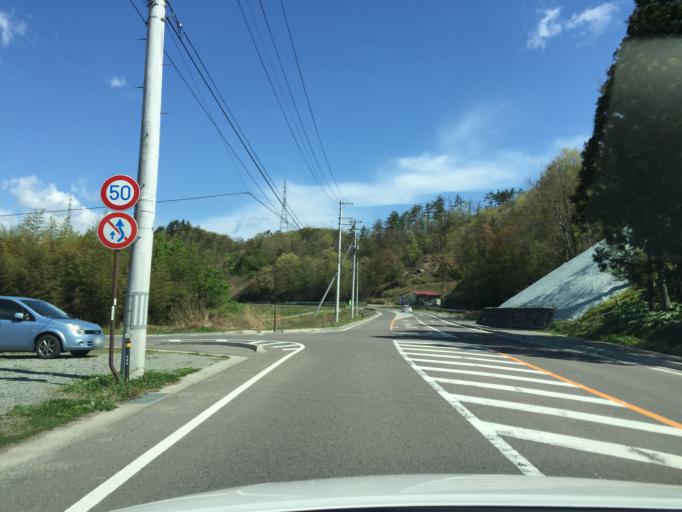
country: JP
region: Fukushima
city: Funehikimachi-funehiki
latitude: 37.5415
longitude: 140.5358
